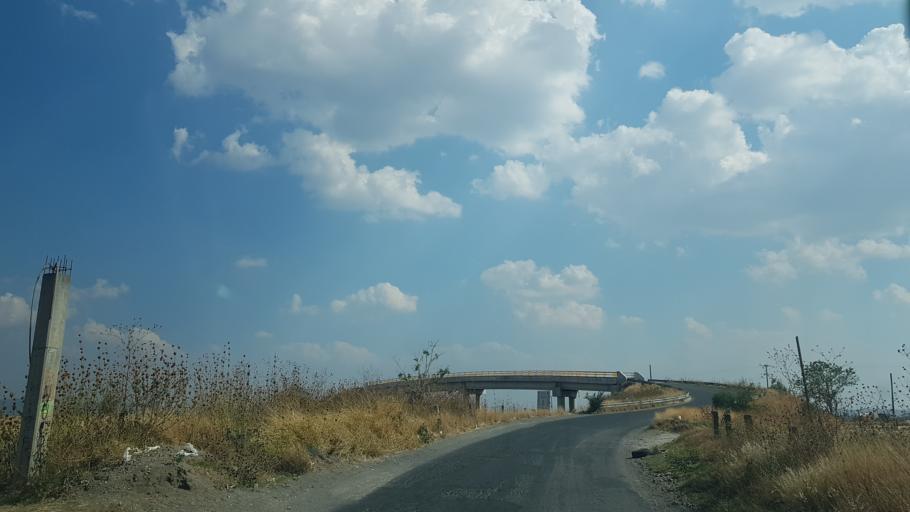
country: MX
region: Puebla
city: Atlixco
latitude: 18.9220
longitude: -98.4829
